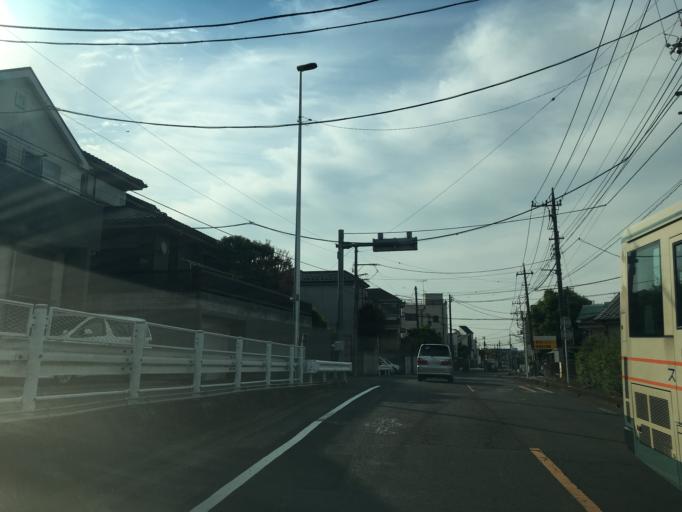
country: JP
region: Saitama
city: Tokorozawa
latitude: 35.7895
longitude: 139.5054
